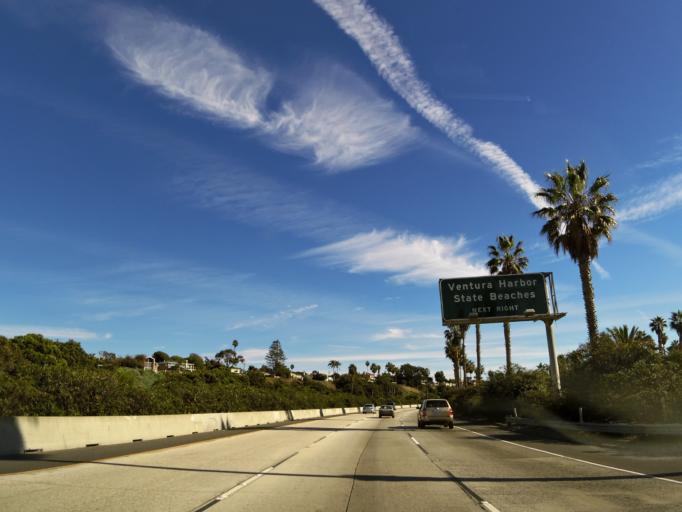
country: US
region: California
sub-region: Ventura County
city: Ventura
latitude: 34.2718
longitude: -119.2782
